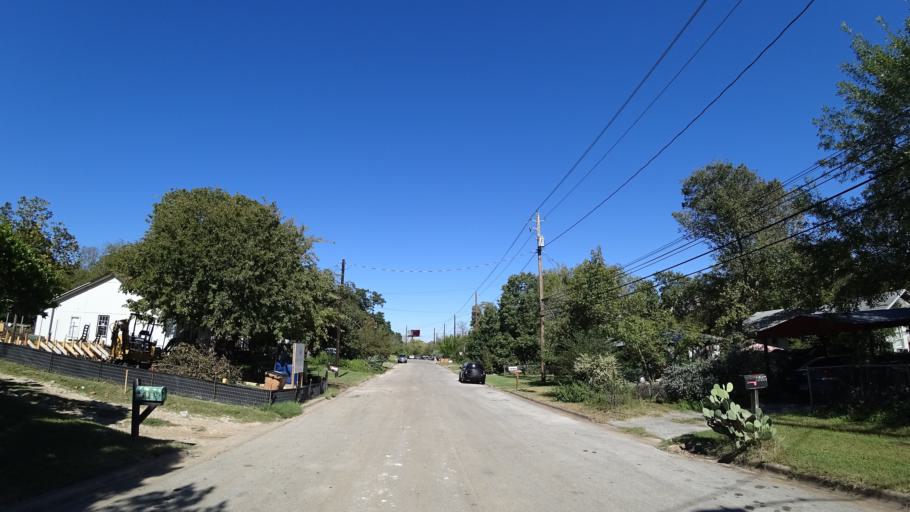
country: US
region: Texas
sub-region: Travis County
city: Rollingwood
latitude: 30.2248
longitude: -97.7783
